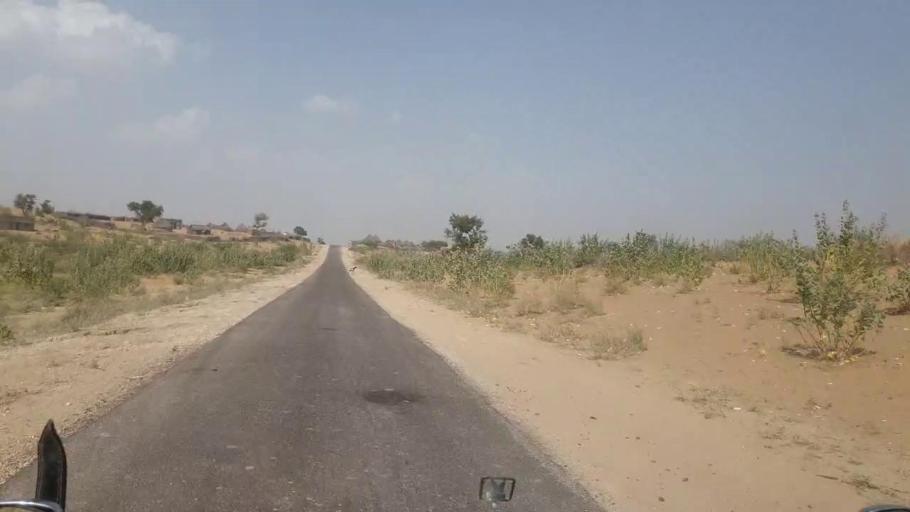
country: PK
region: Sindh
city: Islamkot
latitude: 25.2124
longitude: 70.2840
